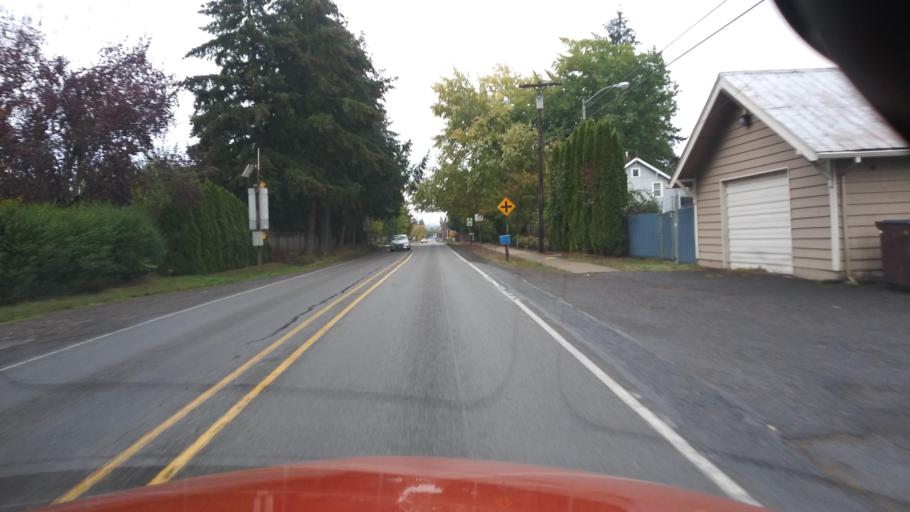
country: US
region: Oregon
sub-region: Washington County
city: Forest Grove
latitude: 45.5497
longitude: -123.0856
